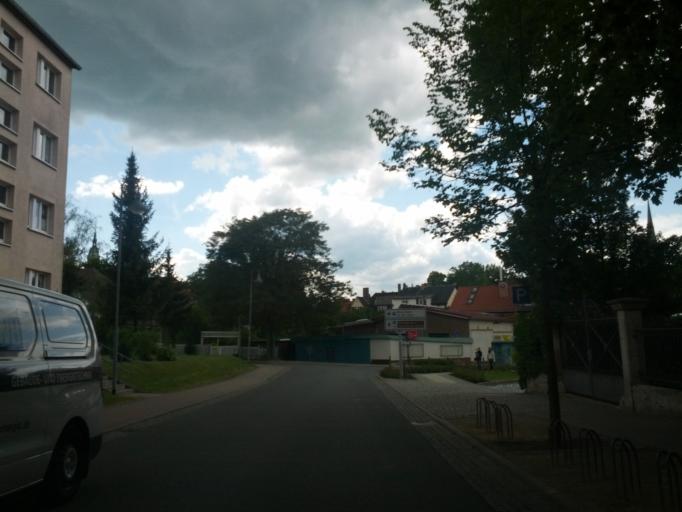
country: DE
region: Thuringia
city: Bad Langensalza
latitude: 51.1108
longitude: 10.6525
